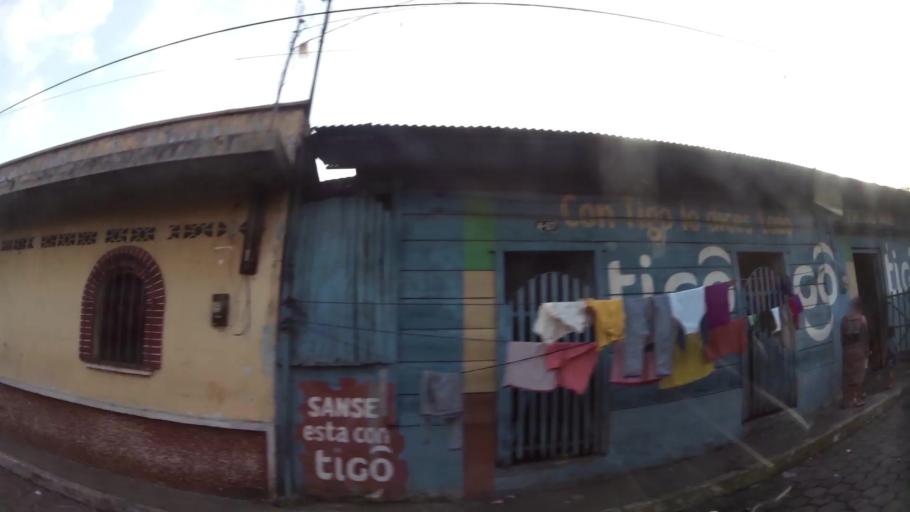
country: GT
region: Retalhuleu
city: San Sebastian
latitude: 14.5593
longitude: -91.6491
